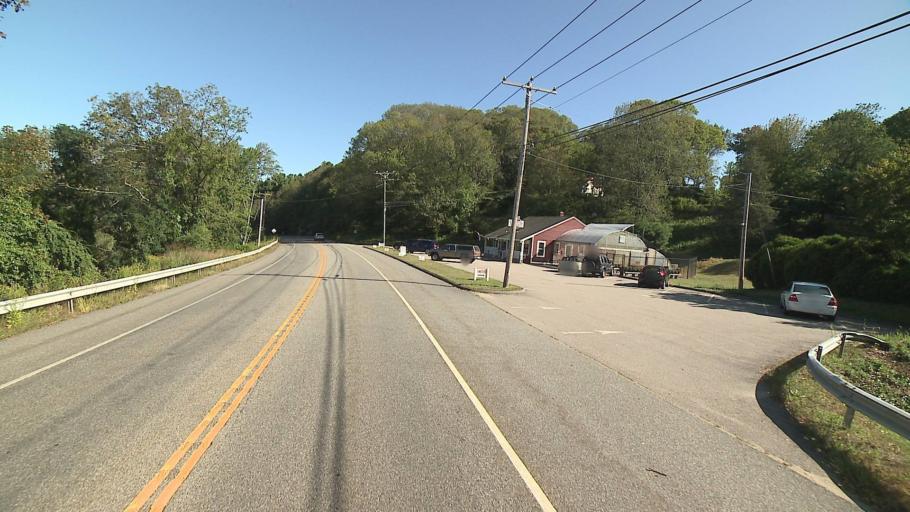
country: US
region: Connecticut
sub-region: New London County
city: Gales Ferry
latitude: 41.4680
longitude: -72.0586
